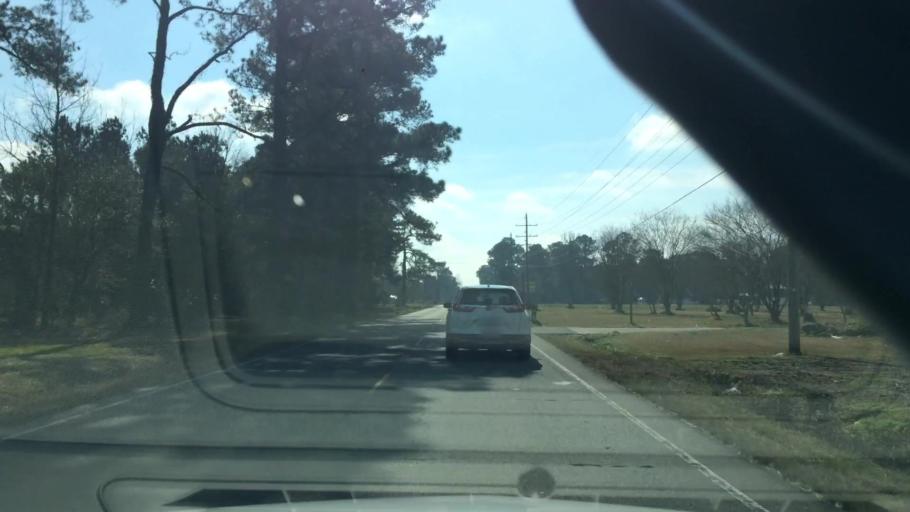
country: US
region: North Carolina
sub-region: Duplin County
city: Beulaville
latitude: 34.9015
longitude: -77.7800
